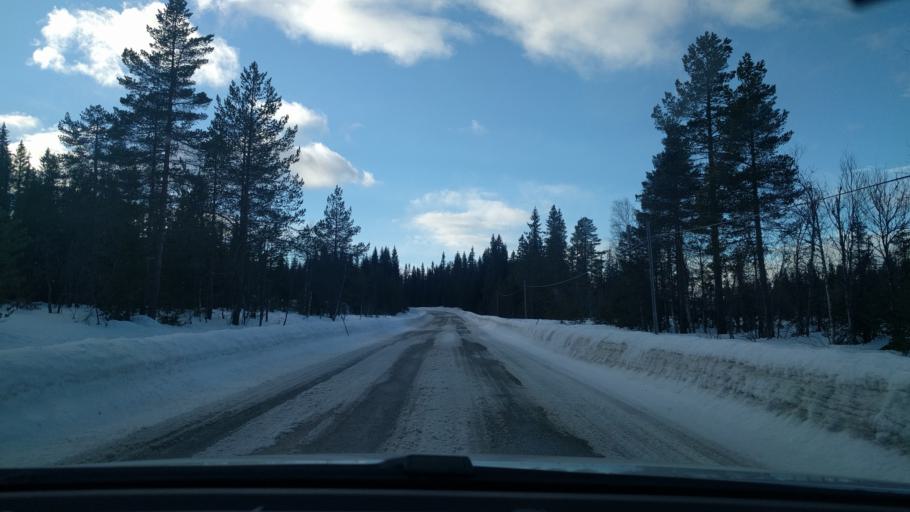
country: NO
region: Hedmark
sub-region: Trysil
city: Innbygda
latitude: 61.1050
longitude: 12.1270
